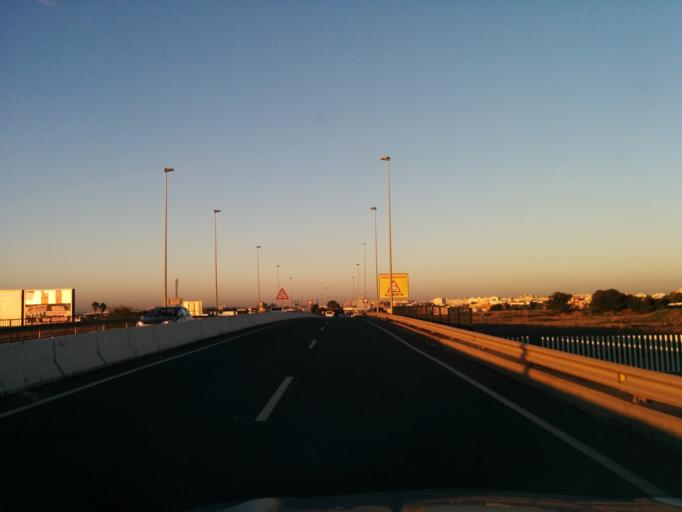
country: ES
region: Andalusia
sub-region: Provincia de Sevilla
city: Sevilla
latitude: 37.3699
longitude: -5.9321
